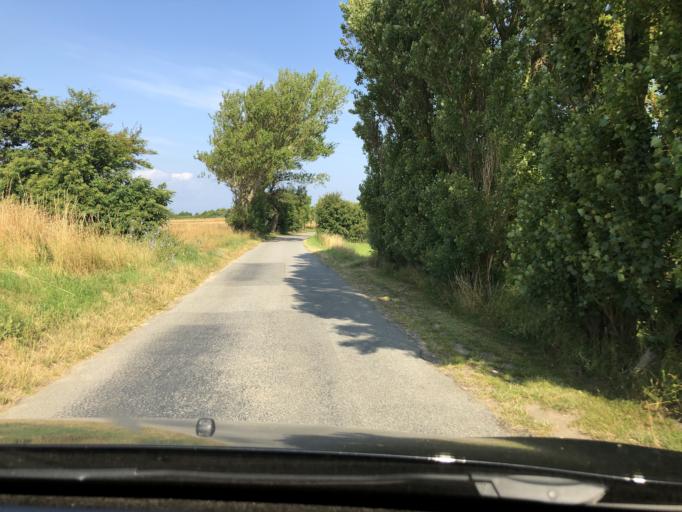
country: DK
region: South Denmark
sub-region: Faaborg-Midtfyn Kommune
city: Faaborg
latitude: 54.9513
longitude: 10.2293
